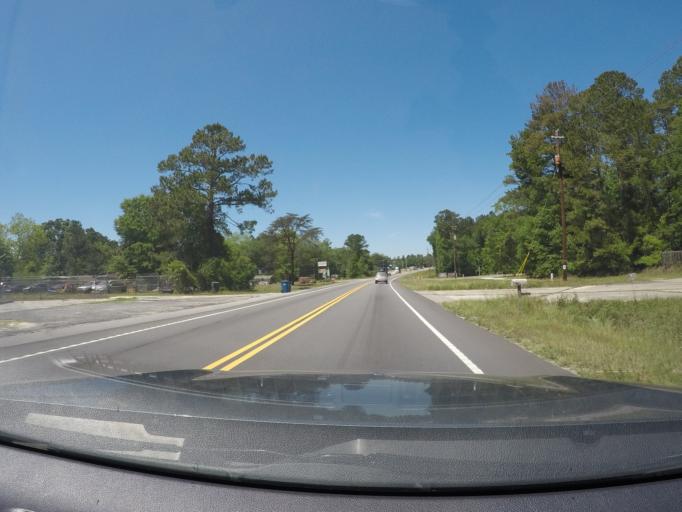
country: US
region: Georgia
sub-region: Effingham County
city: Guyton
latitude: 32.1955
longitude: -81.4340
